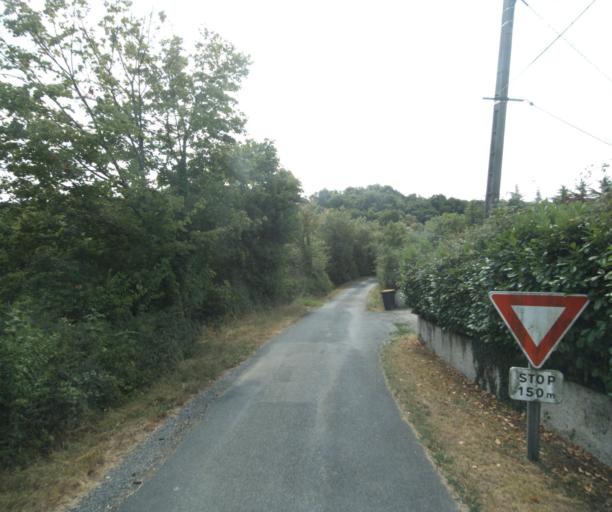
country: FR
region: Rhone-Alpes
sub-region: Departement du Rhone
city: Lentilly
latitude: 45.8328
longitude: 4.6614
